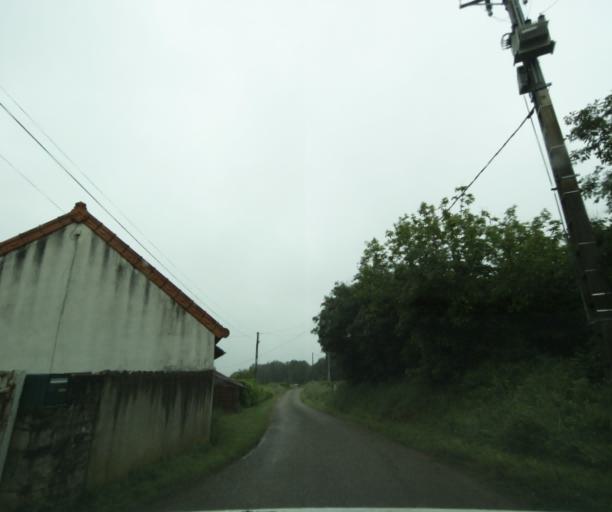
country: FR
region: Bourgogne
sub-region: Departement de Saone-et-Loire
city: Charolles
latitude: 46.4220
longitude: 4.3725
